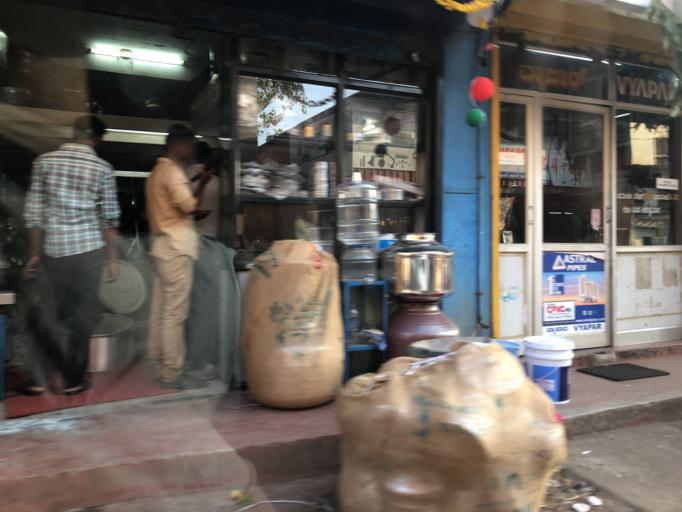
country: IN
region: Karnataka
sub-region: Dakshina Kannada
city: Mangalore
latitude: 12.8656
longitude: 74.8362
